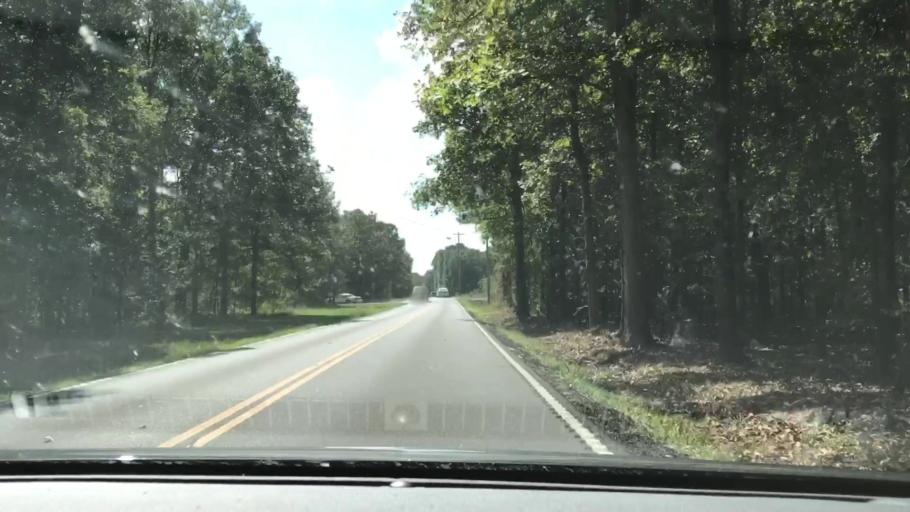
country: US
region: Kentucky
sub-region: McCracken County
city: Reidland
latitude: 36.9612
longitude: -88.5136
